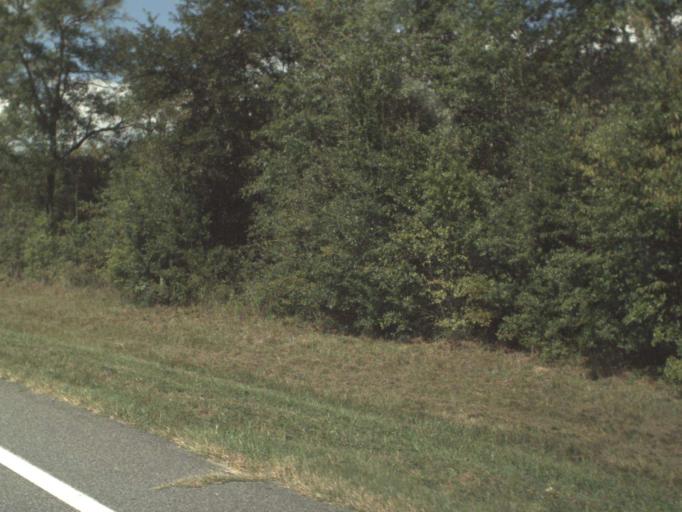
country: US
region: Florida
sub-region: Walton County
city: Freeport
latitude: 30.4726
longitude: -85.9682
